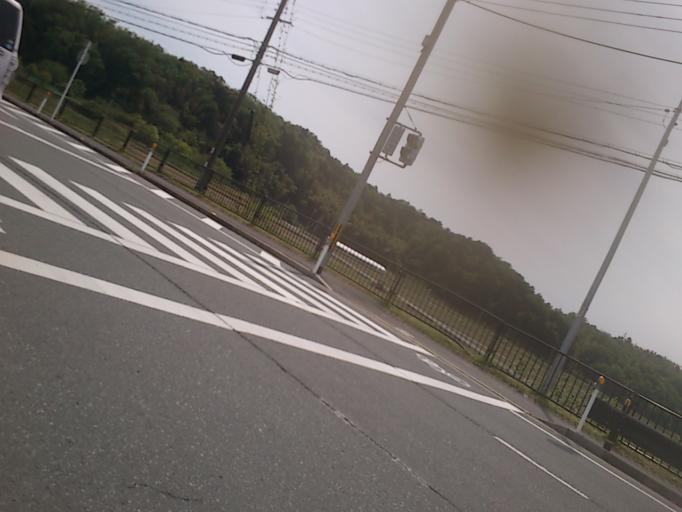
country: JP
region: Kyoto
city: Miyazu
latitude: 35.6400
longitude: 135.0796
